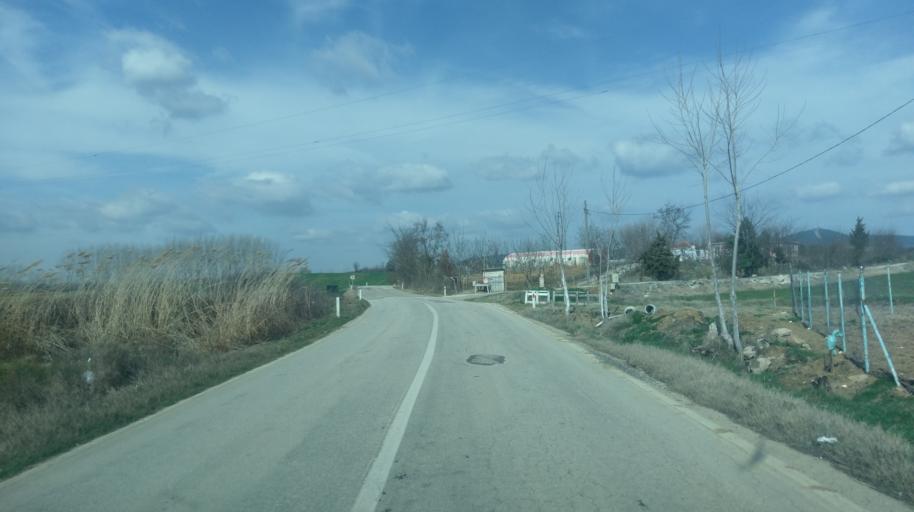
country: TR
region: Edirne
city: Kesan
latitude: 40.7762
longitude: 26.6767
